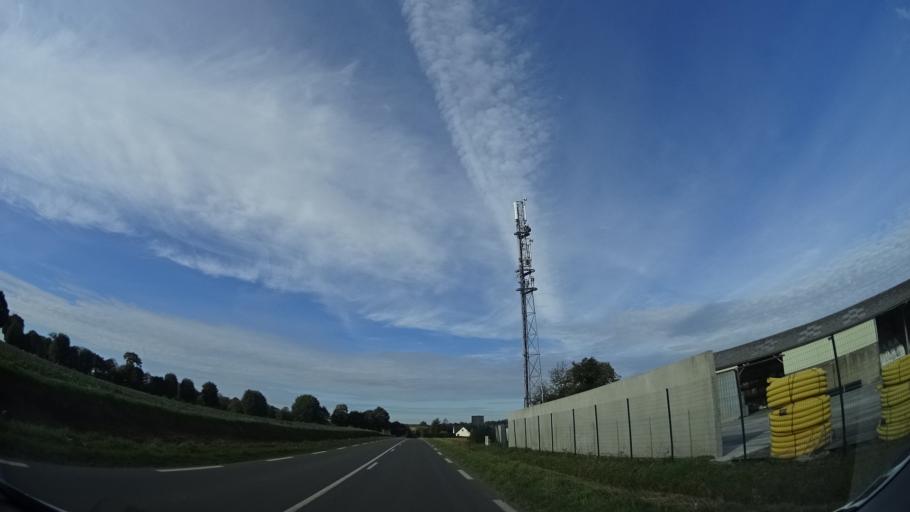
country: FR
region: Brittany
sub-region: Departement d'Ille-et-Vilaine
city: Geveze
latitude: 48.2273
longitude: -1.7978
